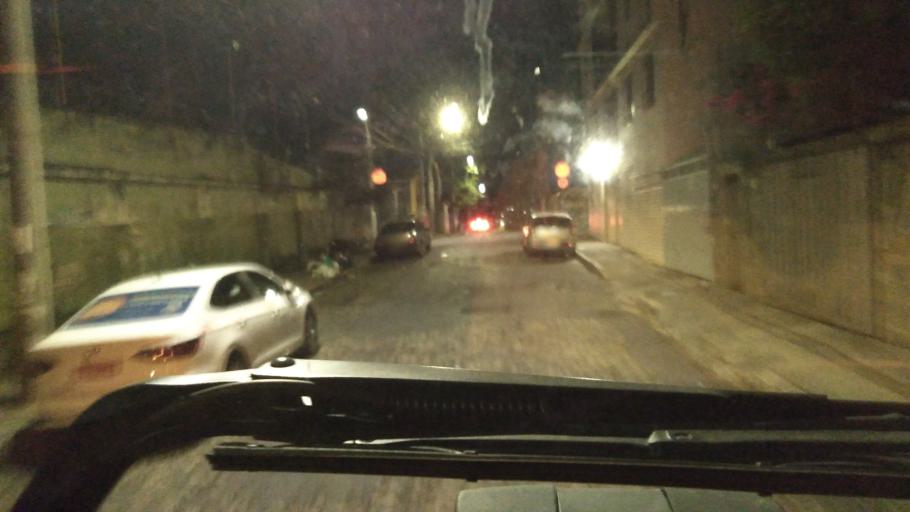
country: BR
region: Minas Gerais
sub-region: Belo Horizonte
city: Belo Horizonte
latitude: -19.9156
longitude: -43.9797
